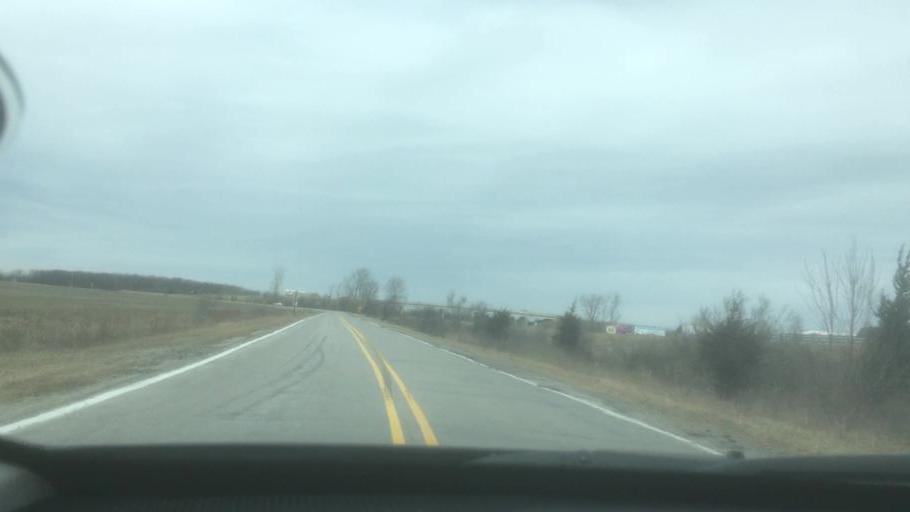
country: US
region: Michigan
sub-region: Bay County
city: Bay City
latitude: 43.6211
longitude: -83.9521
